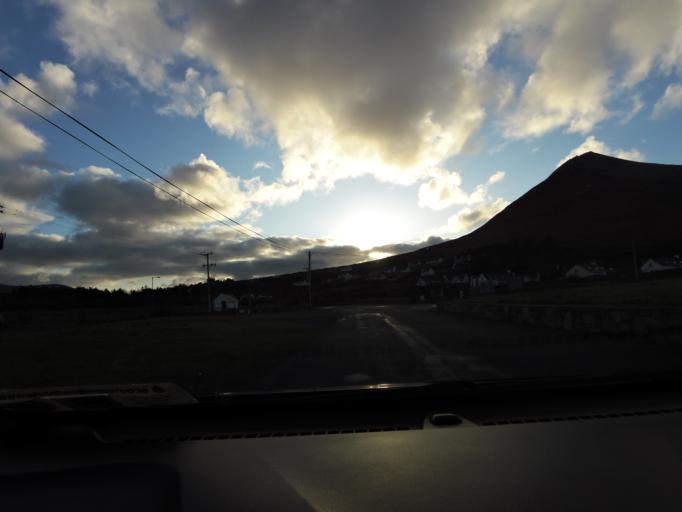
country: IE
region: Connaught
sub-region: Maigh Eo
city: Belmullet
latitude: 54.0099
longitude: -10.0244
